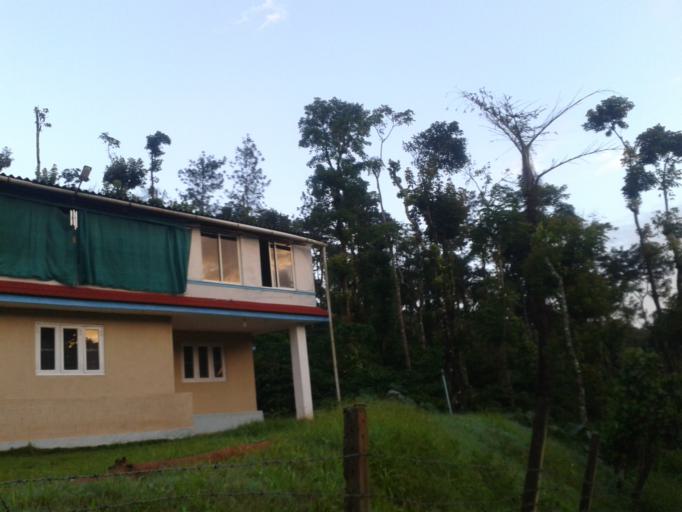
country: IN
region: Karnataka
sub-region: Chikmagalur
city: Mudigere
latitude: 13.0135
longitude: 75.6713
